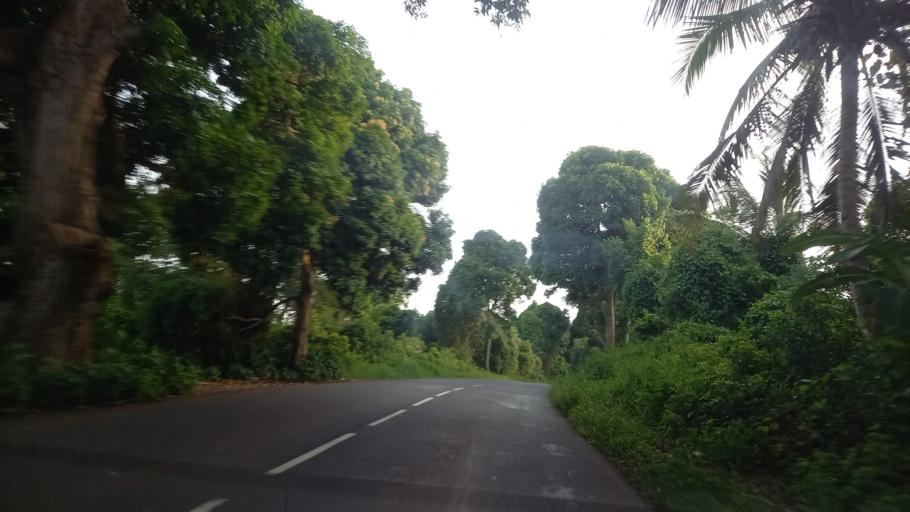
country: YT
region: M'Tsangamouji
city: M'Tsangamouji
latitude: -12.7443
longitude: 45.1152
